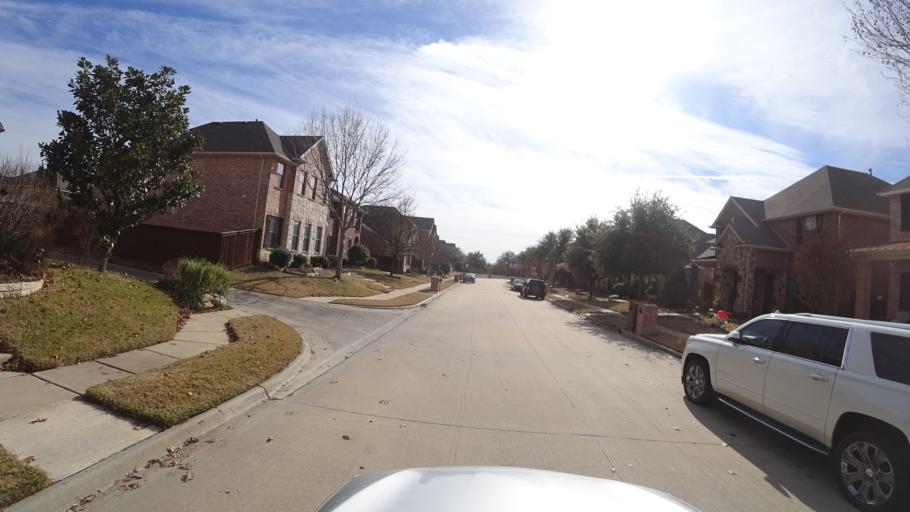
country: US
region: Texas
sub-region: Denton County
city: Highland Village
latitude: 33.0645
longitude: -97.0335
